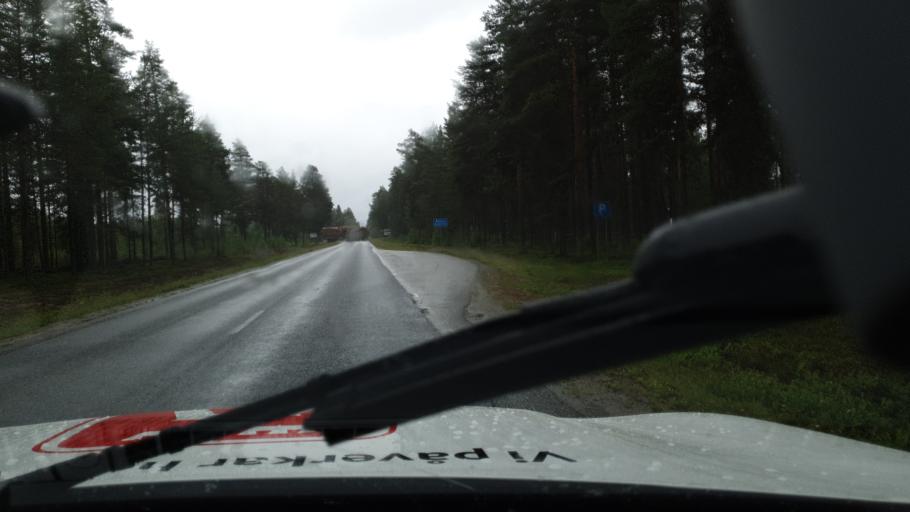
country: SE
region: Vaesterbotten
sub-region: Asele Kommun
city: Asele
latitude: 64.1758
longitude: 17.3588
